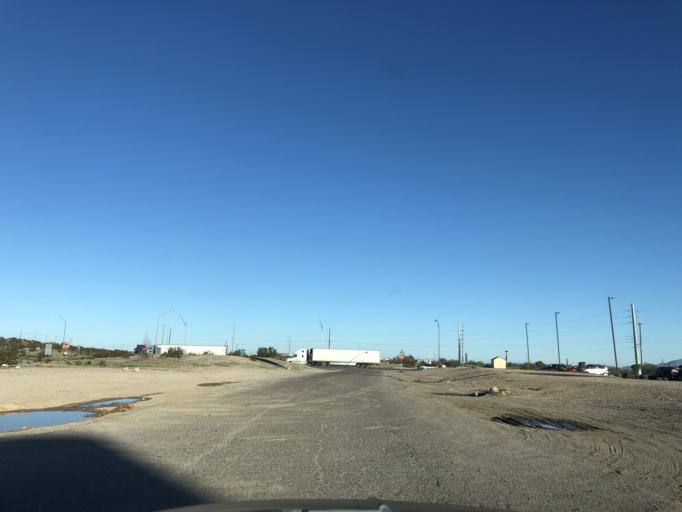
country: US
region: Arizona
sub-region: Maricopa County
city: Buckeye
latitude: 33.4323
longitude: -112.5923
